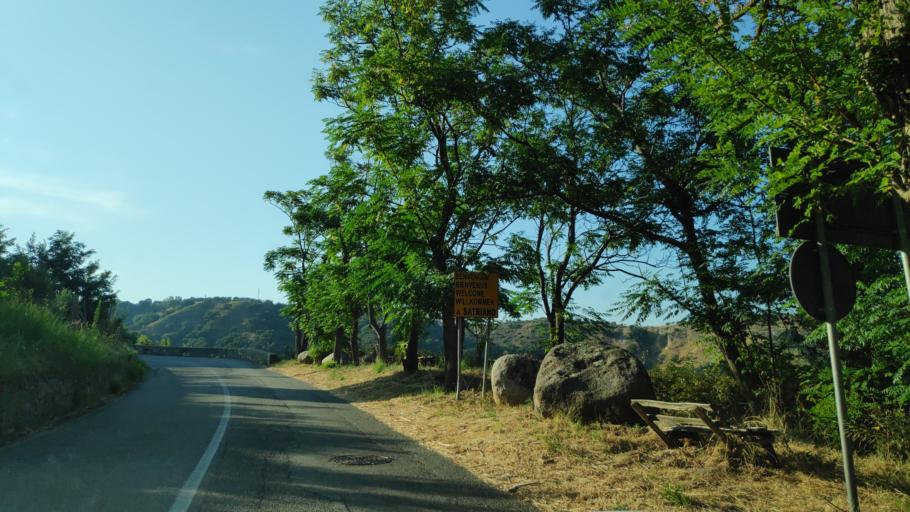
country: IT
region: Calabria
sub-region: Provincia di Catanzaro
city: Satriano
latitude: 38.6704
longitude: 16.4830
